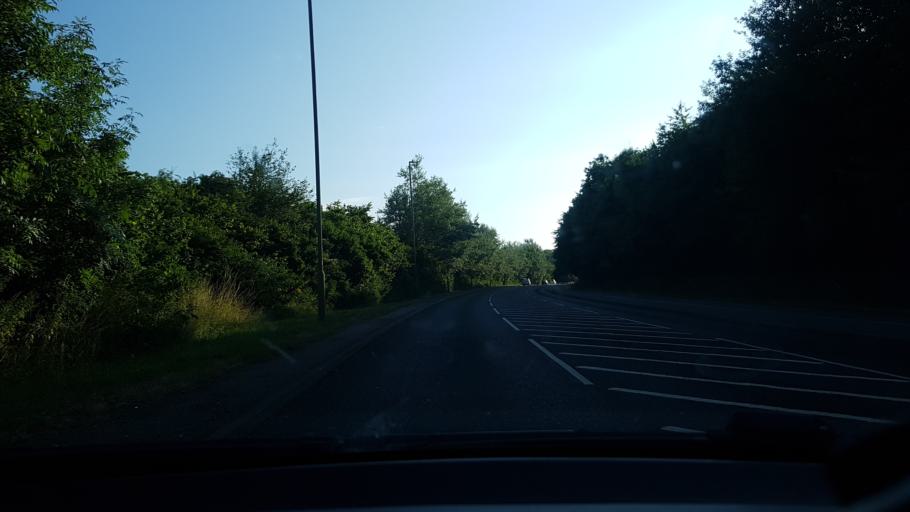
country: GB
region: England
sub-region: Nottinghamshire
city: Awsworth
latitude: 52.9932
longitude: -1.2904
